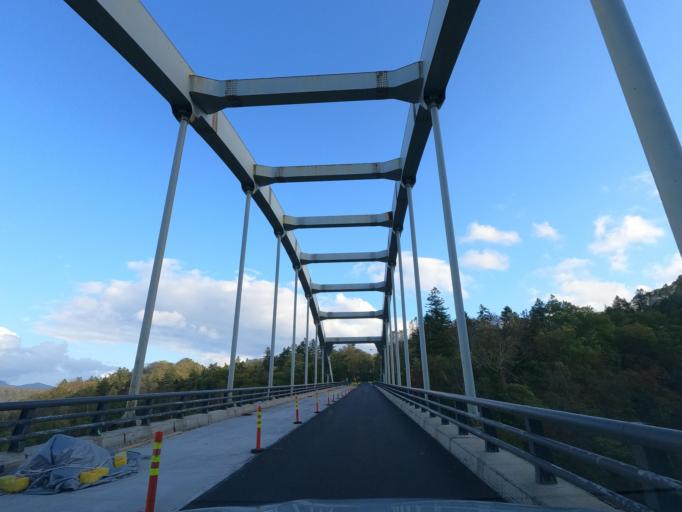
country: JP
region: Hokkaido
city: Shiraoi
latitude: 42.7167
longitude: 141.2075
